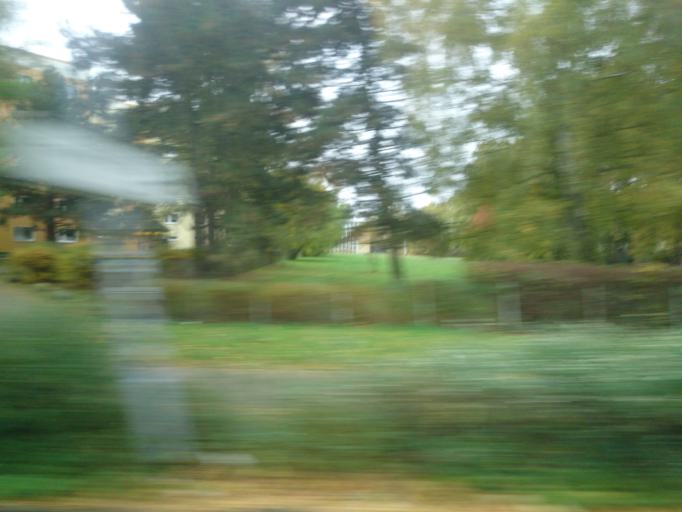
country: DE
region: Mecklenburg-Vorpommern
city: Rostock
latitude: 54.0769
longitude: 12.1179
